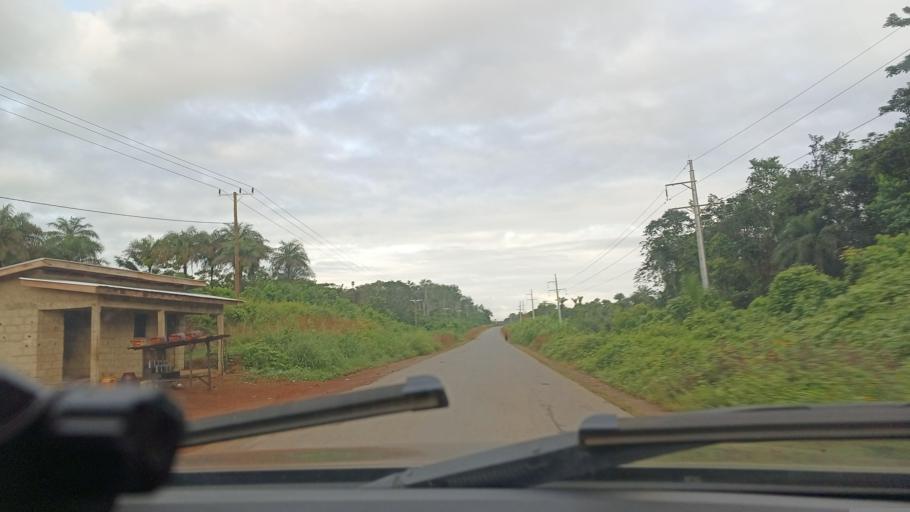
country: LR
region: Montserrado
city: Monrovia
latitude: 6.5531
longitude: -10.8651
